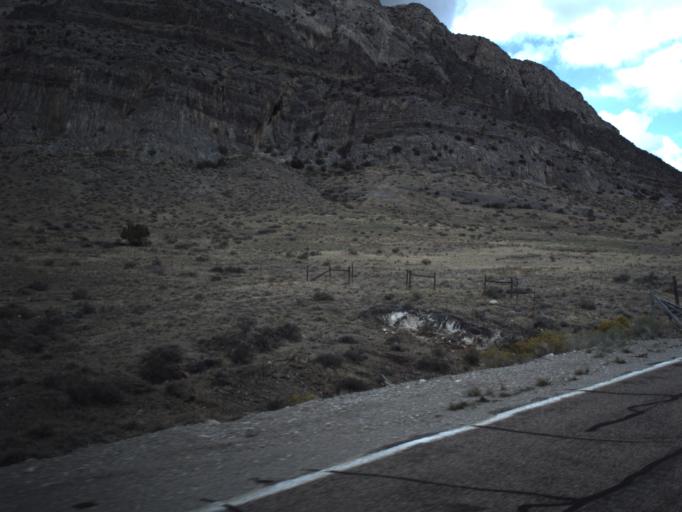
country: US
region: Utah
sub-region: Beaver County
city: Milford
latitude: 38.5059
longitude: -113.6032
